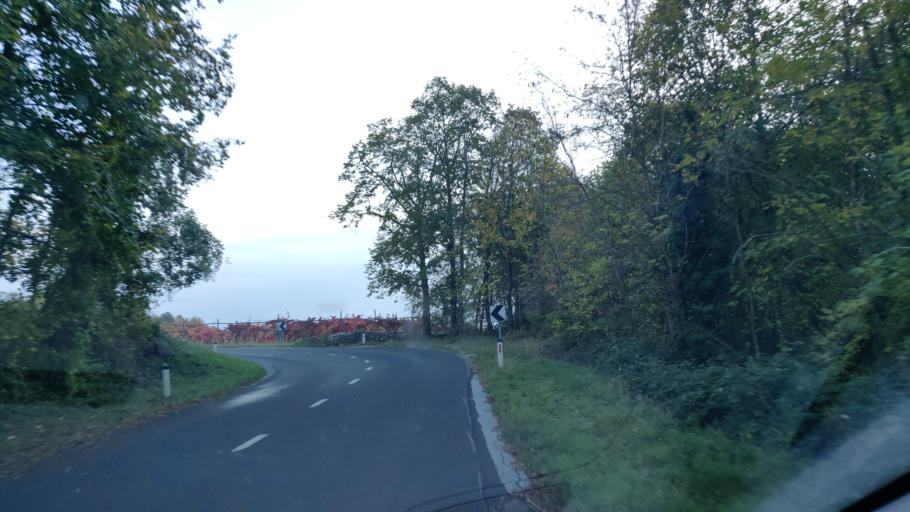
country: SI
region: Sezana
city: Sezana
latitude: 45.7921
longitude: 13.8586
